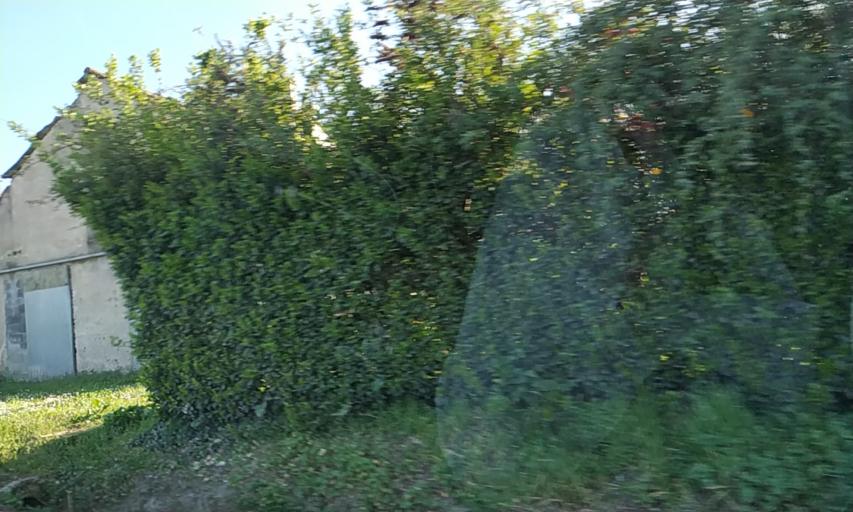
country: ES
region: Galicia
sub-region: Provincia de Lugo
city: Corgo
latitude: 42.9564
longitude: -7.4688
